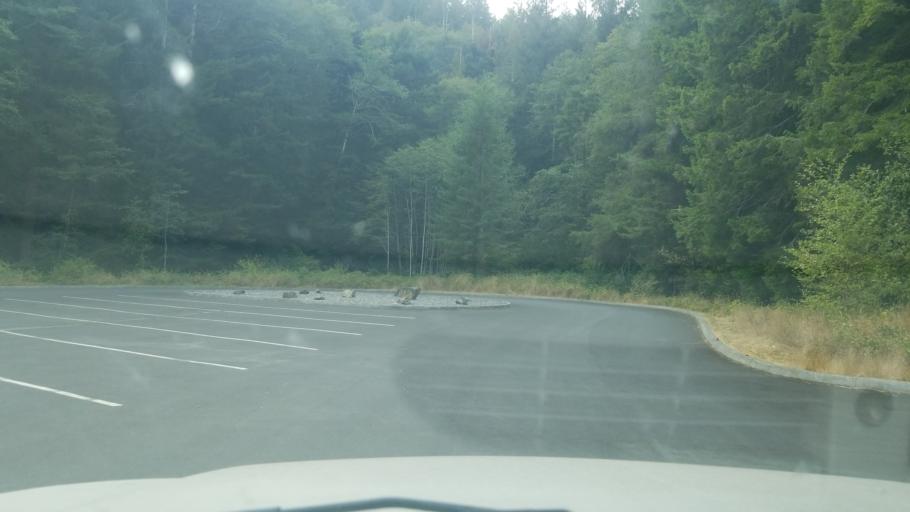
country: US
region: California
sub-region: Humboldt County
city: Westhaven-Moonstone
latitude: 41.3232
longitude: -124.0455
